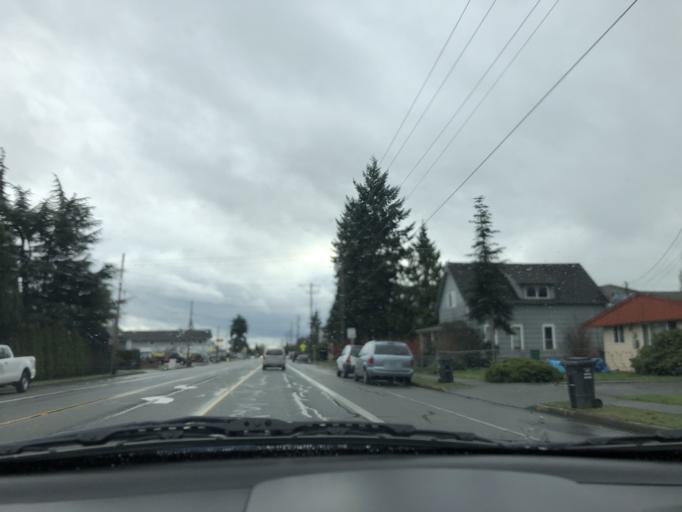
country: US
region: Washington
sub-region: Snohomish County
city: Marysville
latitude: 48.0572
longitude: -122.1805
